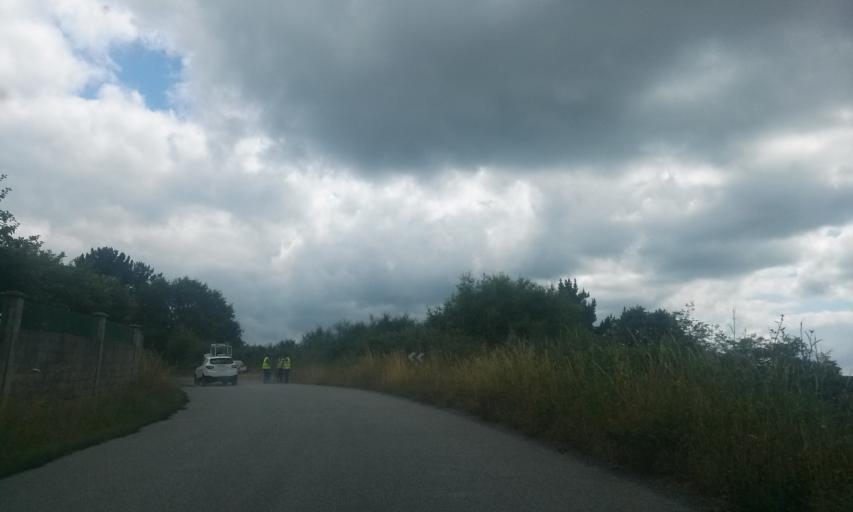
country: ES
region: Galicia
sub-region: Provincia de Lugo
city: Outeiro de Rei
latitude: 43.0641
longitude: -7.6160
